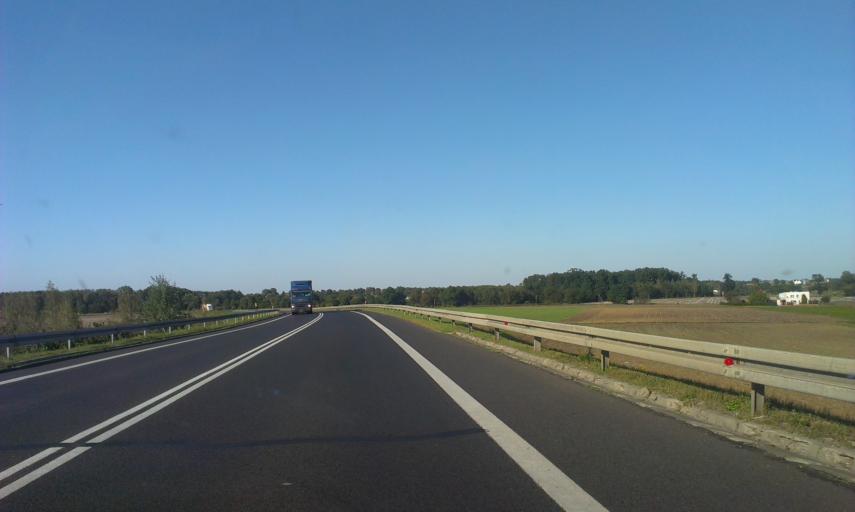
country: PL
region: Kujawsko-Pomorskie
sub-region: Powiat torunski
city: Chelmza
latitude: 53.1990
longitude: 18.5659
